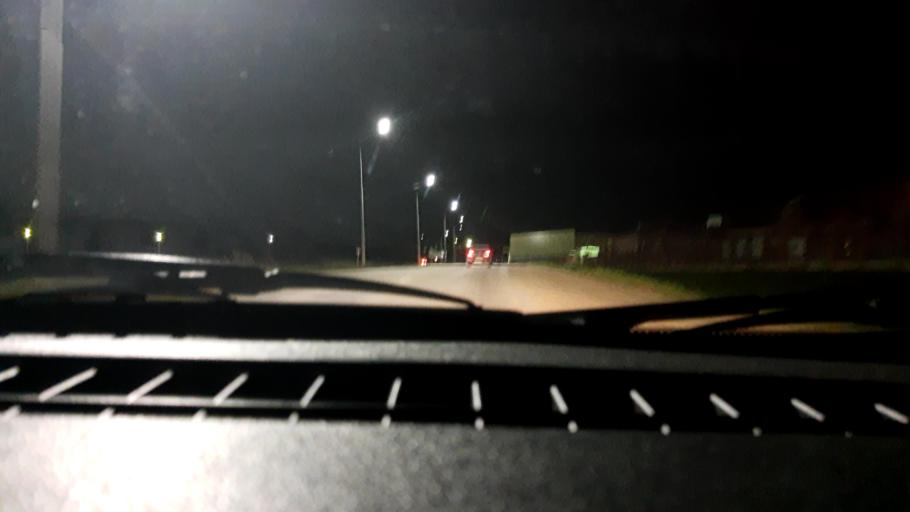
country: RU
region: Bashkortostan
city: Mikhaylovka
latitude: 54.8335
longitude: 55.8202
